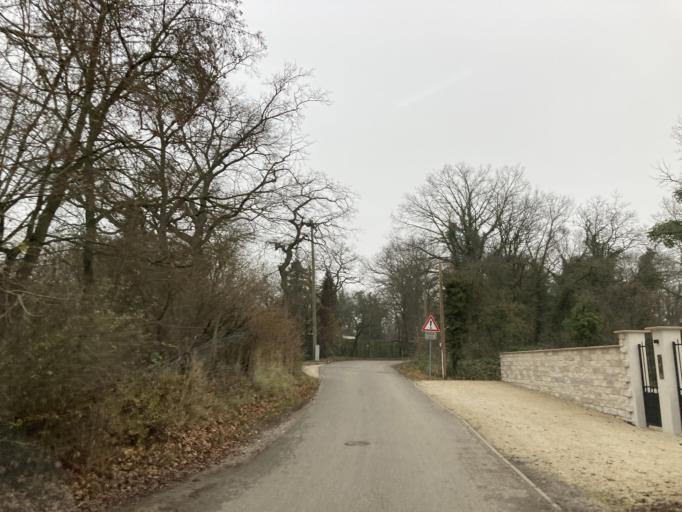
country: DE
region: Baden-Wuerttemberg
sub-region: Freiburg Region
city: Neuenburg am Rhein
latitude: 47.7927
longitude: 7.5458
